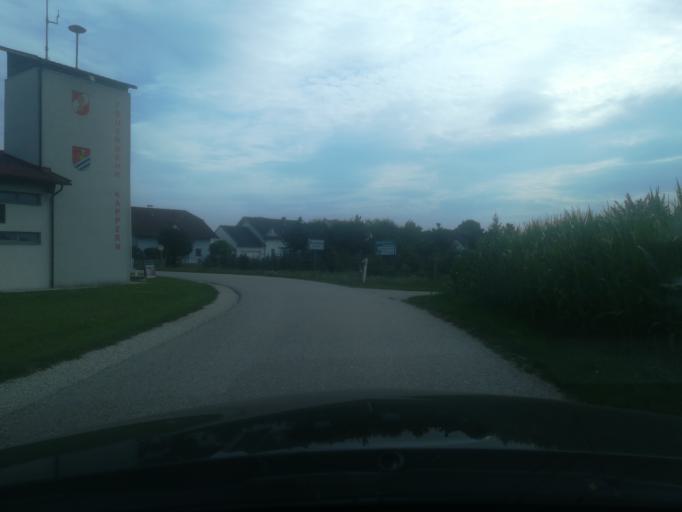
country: AT
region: Upper Austria
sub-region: Wels-Land
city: Marchtrenk
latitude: 48.1899
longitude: 14.1294
